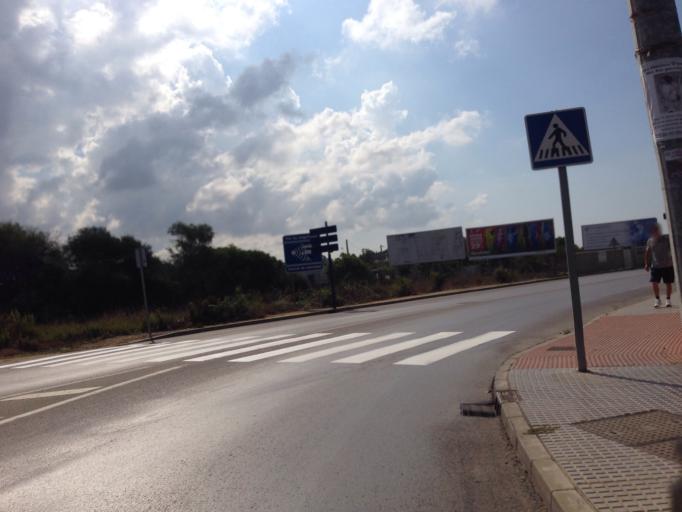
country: ES
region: Andalusia
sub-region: Provincia de Cadiz
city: Chiclana de la Frontera
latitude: 36.4071
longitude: -6.1661
